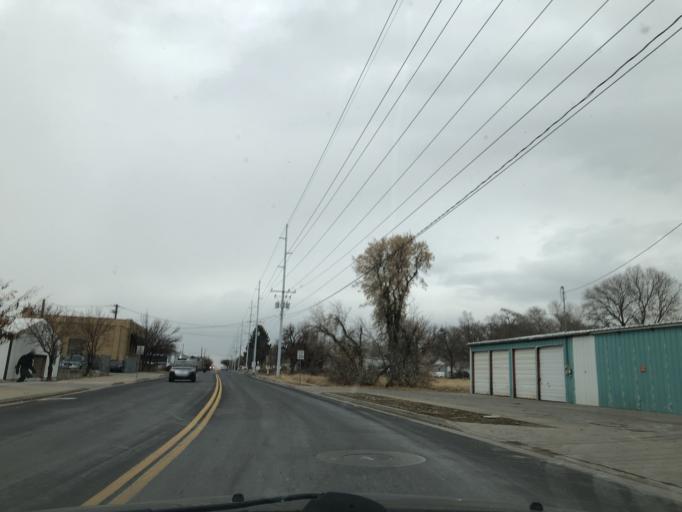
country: US
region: Utah
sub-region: Cache County
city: Logan
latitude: 41.7269
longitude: -111.8500
